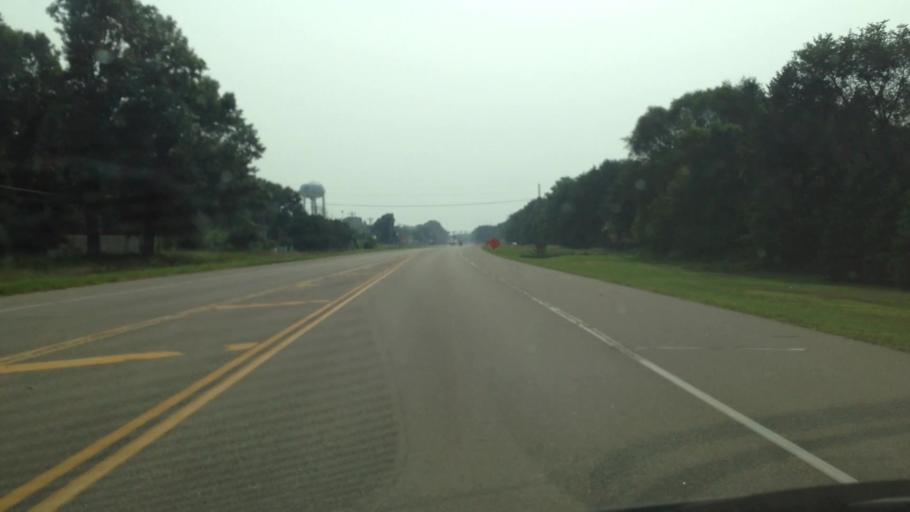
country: US
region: Minnesota
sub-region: Anoka County
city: Circle Pines
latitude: 45.1500
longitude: -93.1440
